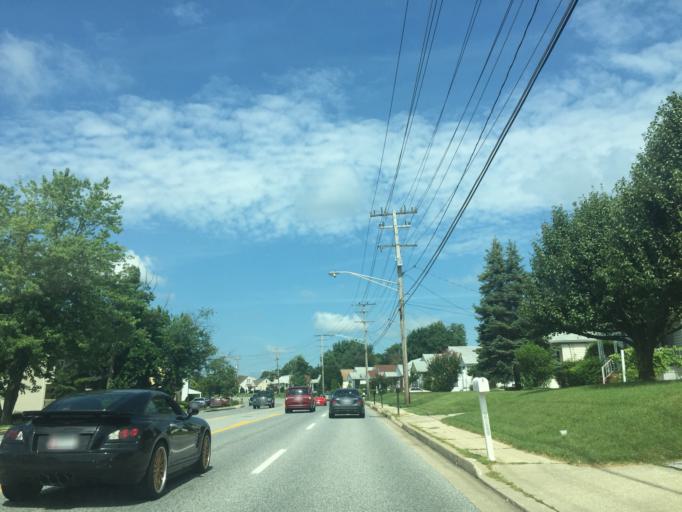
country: US
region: Maryland
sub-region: Baltimore County
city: Carney
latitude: 39.3976
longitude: -76.5318
